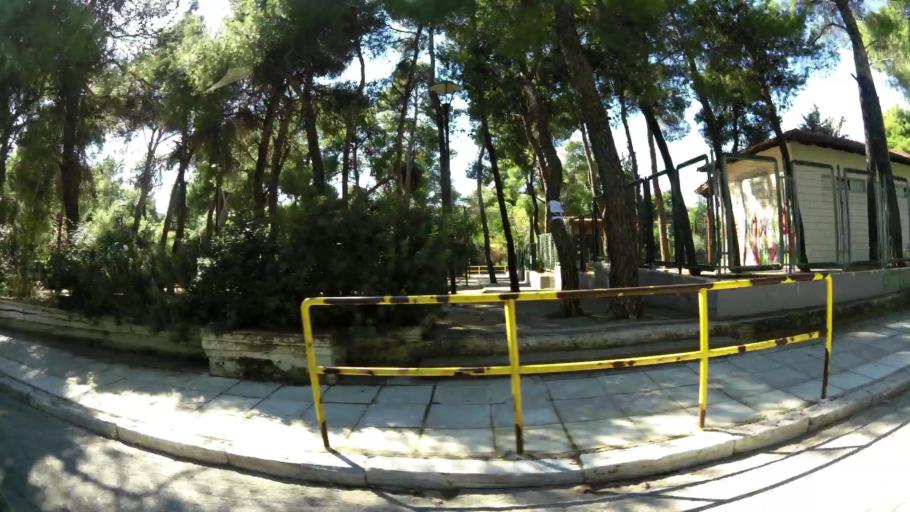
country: GR
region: Attica
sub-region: Nomarchia Athinas
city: Ekali
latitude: 38.1106
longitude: 23.8377
